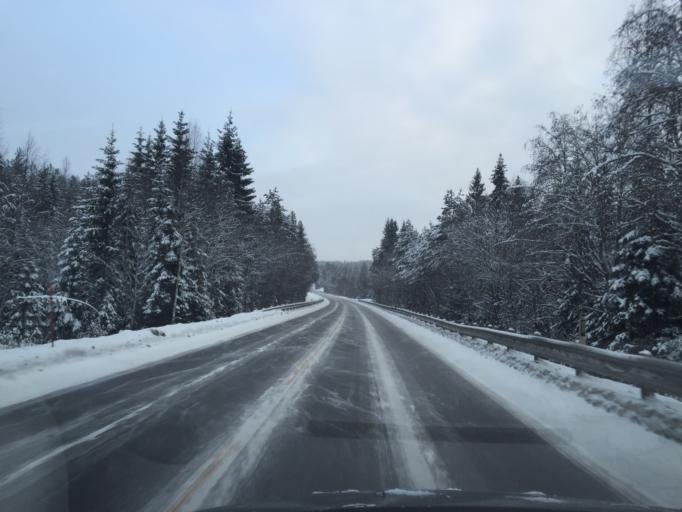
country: NO
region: Hedmark
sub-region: Elverum
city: Elverum
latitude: 60.9481
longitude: 11.6952
